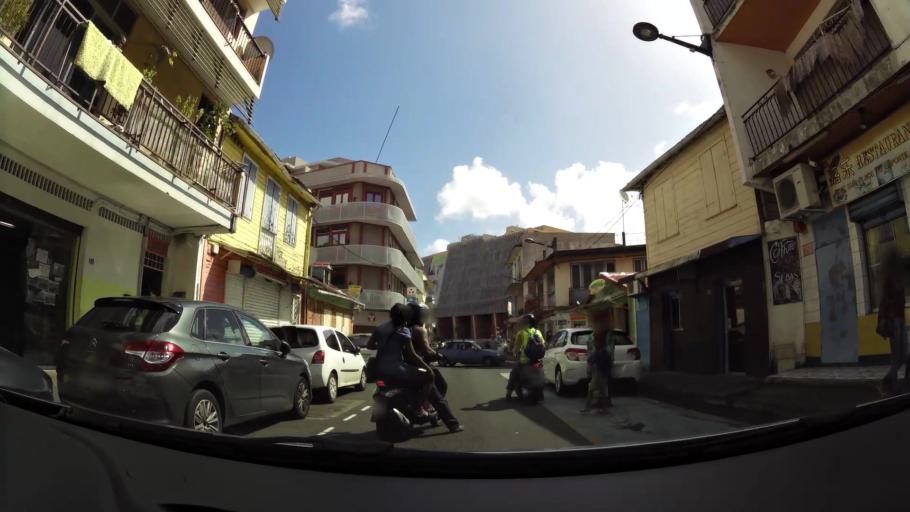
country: MQ
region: Martinique
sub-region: Martinique
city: Fort-de-France
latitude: 14.6084
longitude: -61.0700
